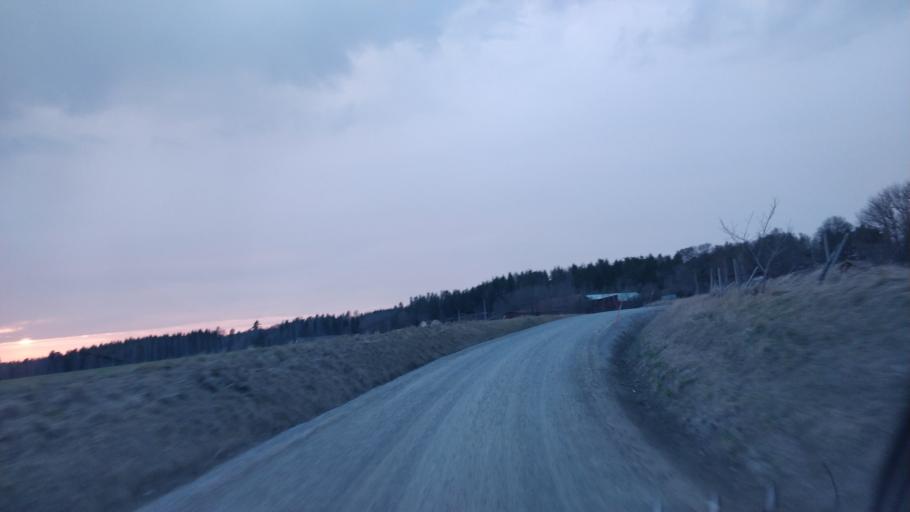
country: SE
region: Uppsala
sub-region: Enkopings Kommun
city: Orsundsbro
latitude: 59.7528
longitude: 17.1719
